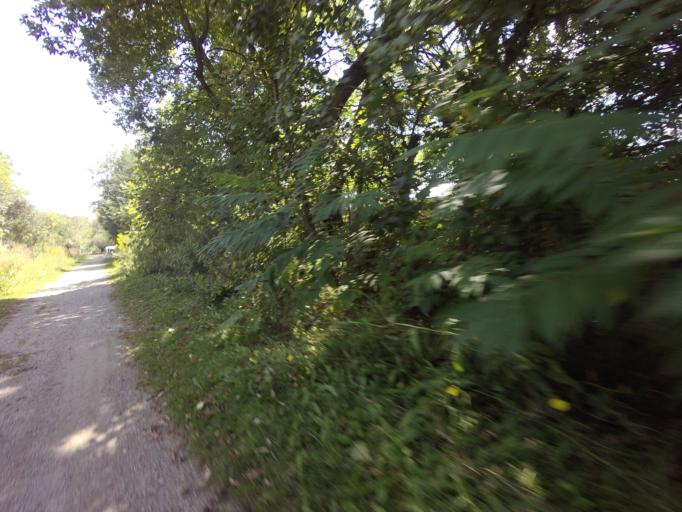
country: CA
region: Ontario
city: Orangeville
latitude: 43.7826
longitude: -80.1311
